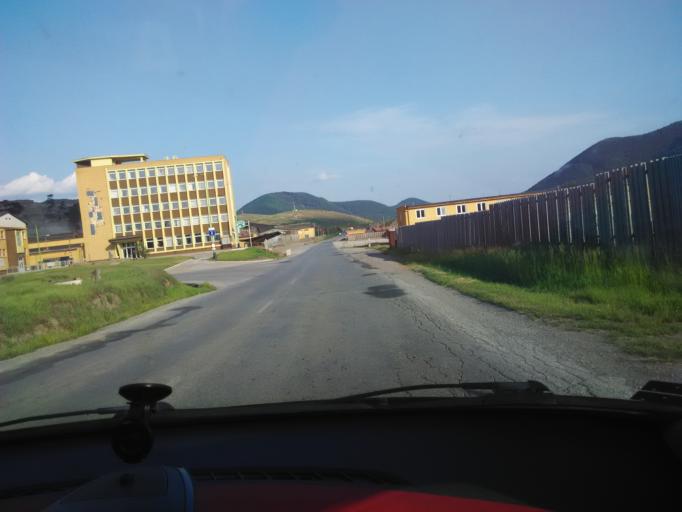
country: SK
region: Banskobystricky
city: Revuca
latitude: 48.6447
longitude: 20.2155
